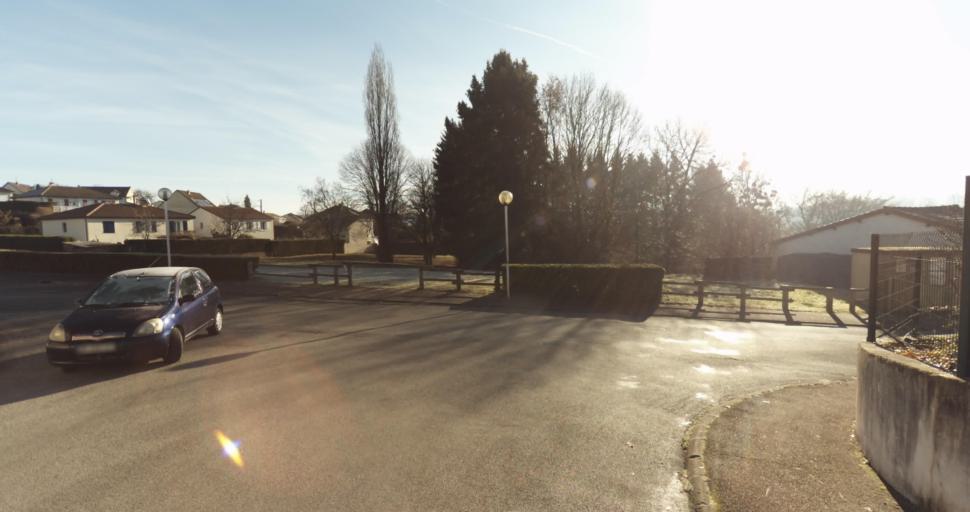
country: FR
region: Limousin
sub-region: Departement de la Haute-Vienne
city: Aixe-sur-Vienne
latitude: 45.8038
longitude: 1.1575
